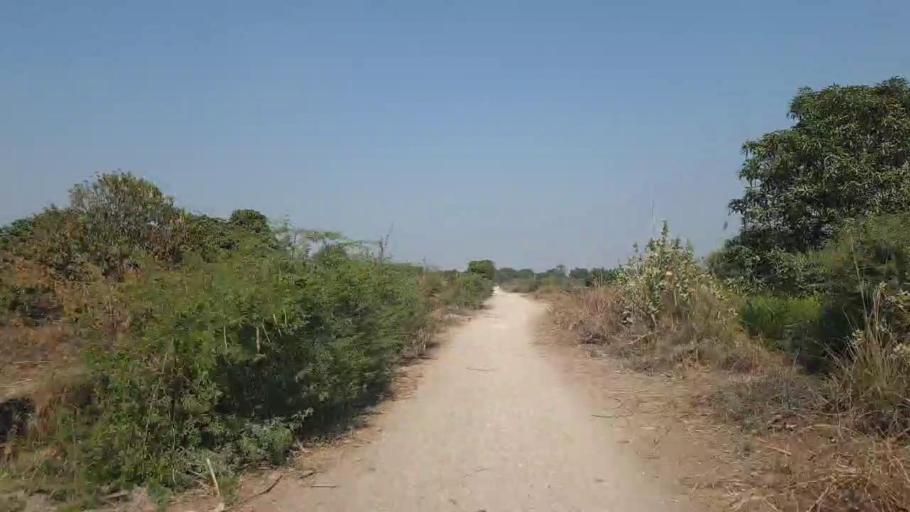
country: PK
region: Sindh
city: Chambar
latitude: 25.4123
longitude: 68.9069
